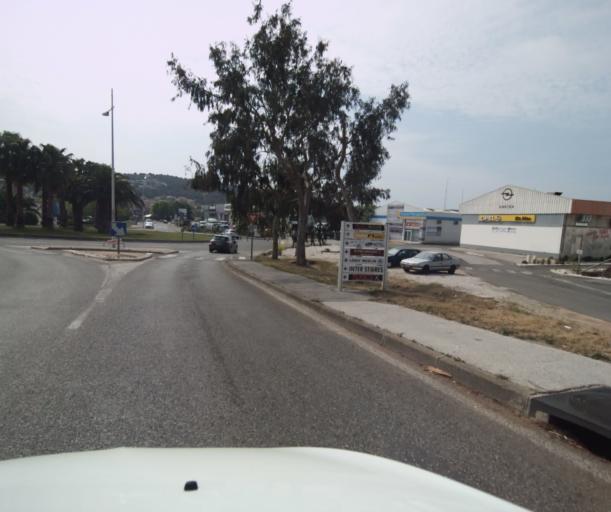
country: FR
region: Provence-Alpes-Cote d'Azur
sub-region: Departement du Var
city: La Garde
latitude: 43.1390
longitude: 6.0023
